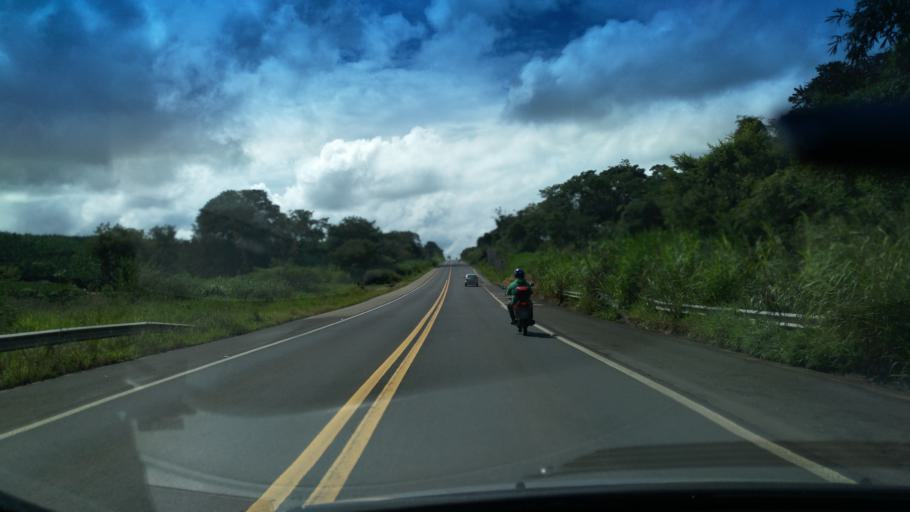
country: BR
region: Sao Paulo
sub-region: Santo Antonio Do Jardim
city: Espirito Santo do Pinhal
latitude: -22.1082
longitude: -46.6750
